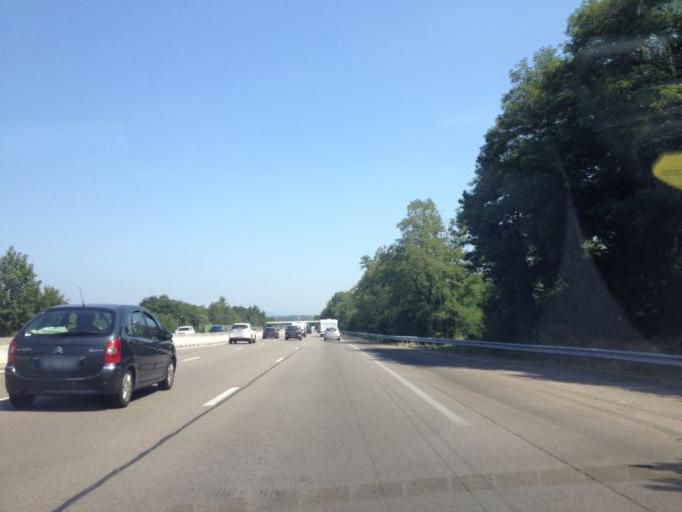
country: FR
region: Rhone-Alpes
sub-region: Departement de l'Ardeche
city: Cruas
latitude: 44.6590
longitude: 4.7962
